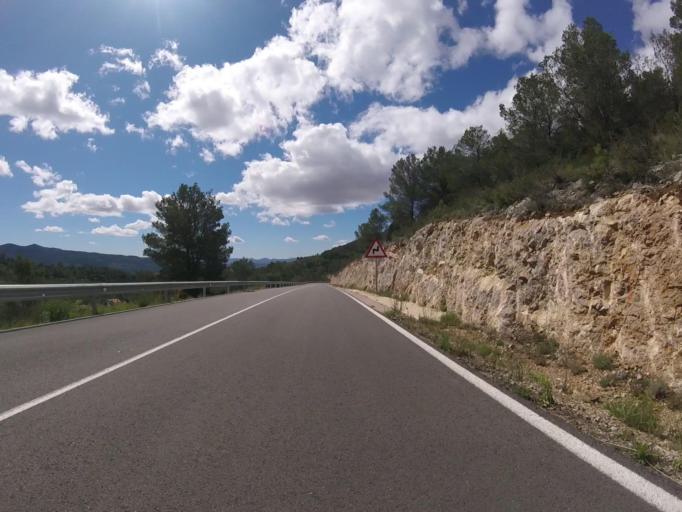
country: ES
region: Valencia
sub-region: Provincia de Castello
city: Adzaneta
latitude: 40.2737
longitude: -0.1102
